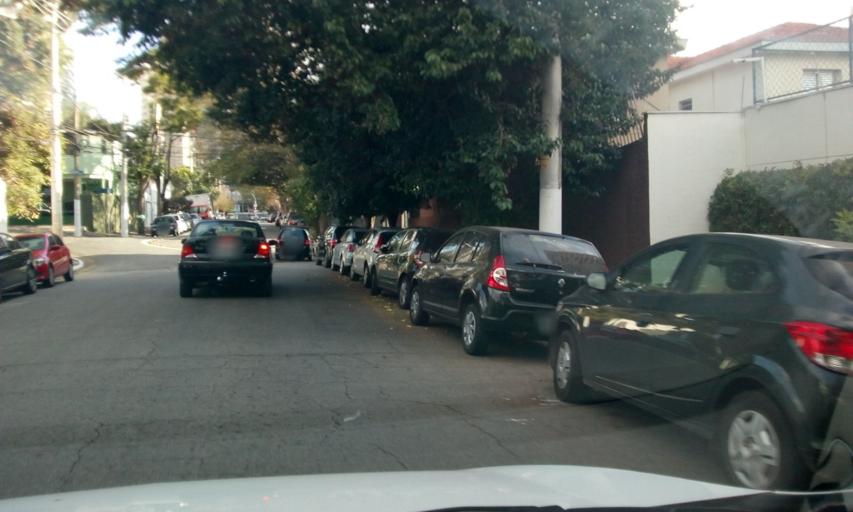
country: BR
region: Sao Paulo
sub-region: Sao Paulo
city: Sao Paulo
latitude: -23.6176
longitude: -46.6944
